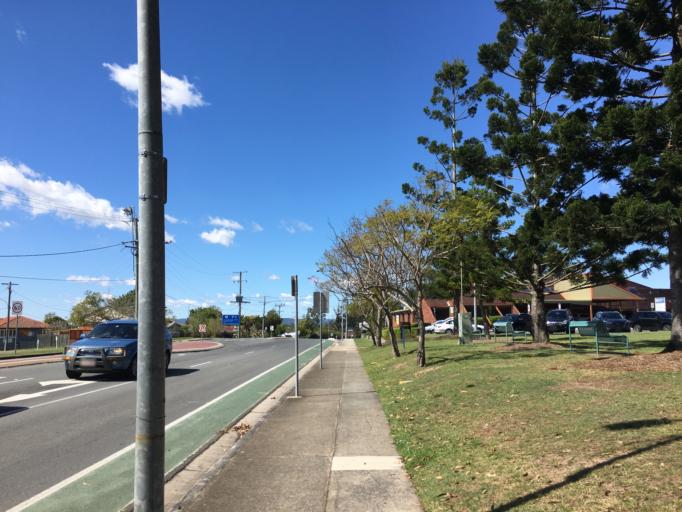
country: AU
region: Queensland
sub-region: Logan
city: Logan City
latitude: -27.6420
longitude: 153.1052
